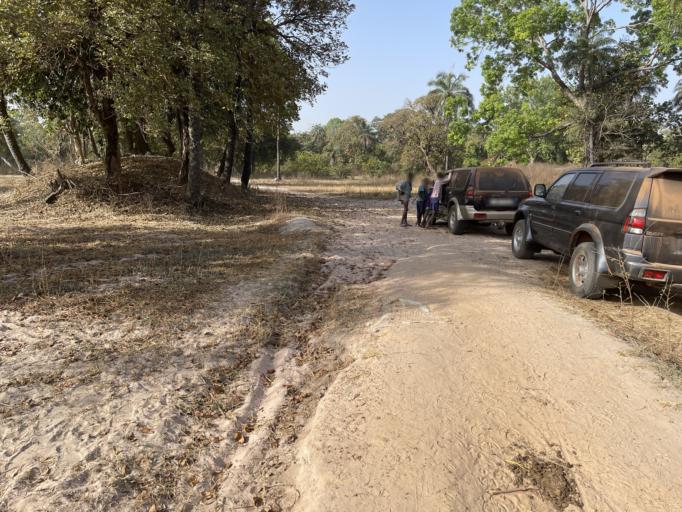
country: GW
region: Oio
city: Farim
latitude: 12.4901
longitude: -15.4076
